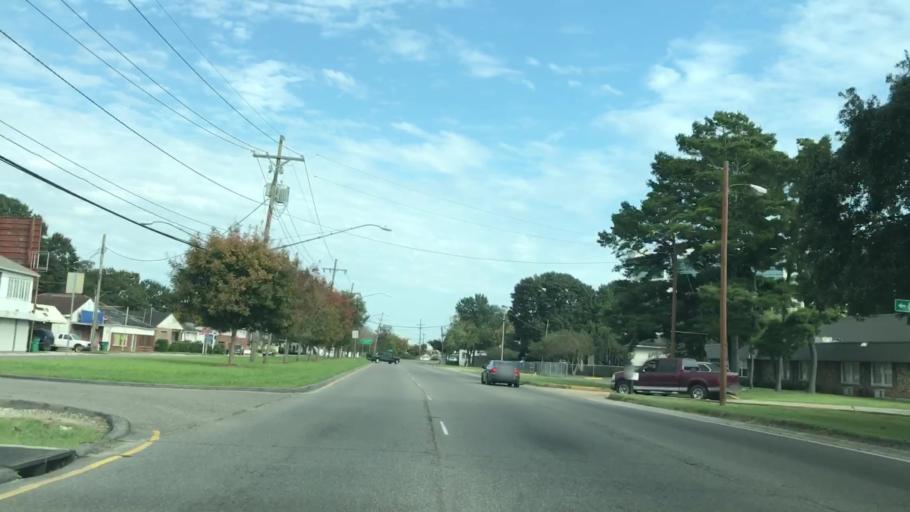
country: US
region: Louisiana
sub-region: Jefferson Parish
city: Jefferson
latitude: 29.9629
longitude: -90.1515
